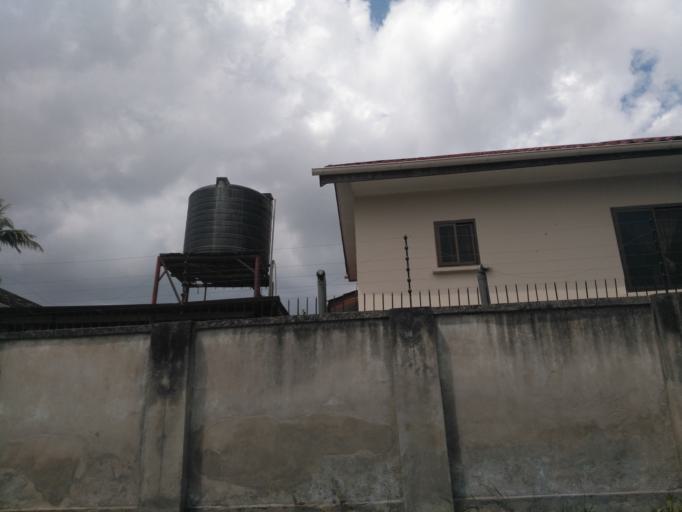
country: TZ
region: Dar es Salaam
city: Magomeni
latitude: -6.7619
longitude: 39.2483
